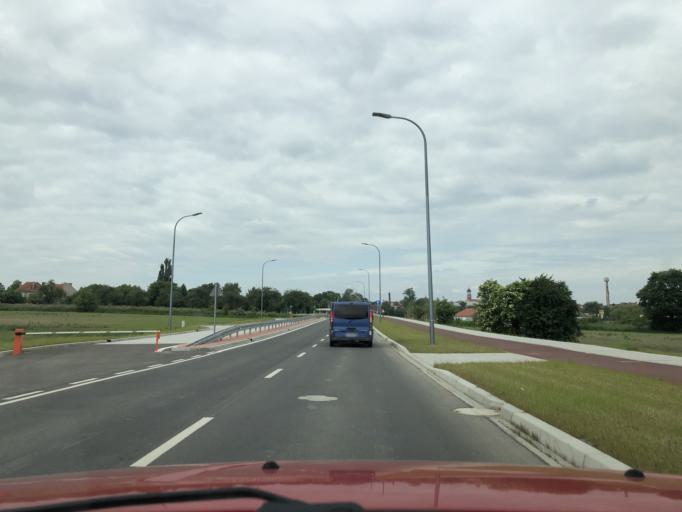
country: PL
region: Greater Poland Voivodeship
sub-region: Powiat jarocinski
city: Jarocin
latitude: 51.9682
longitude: 17.5120
